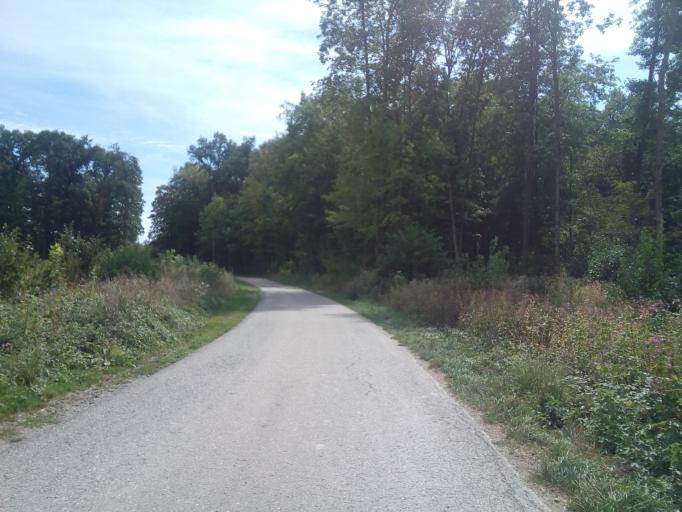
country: DE
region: Baden-Wuerttemberg
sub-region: Karlsruhe Region
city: Lichtenau
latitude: 48.7022
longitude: 8.0171
